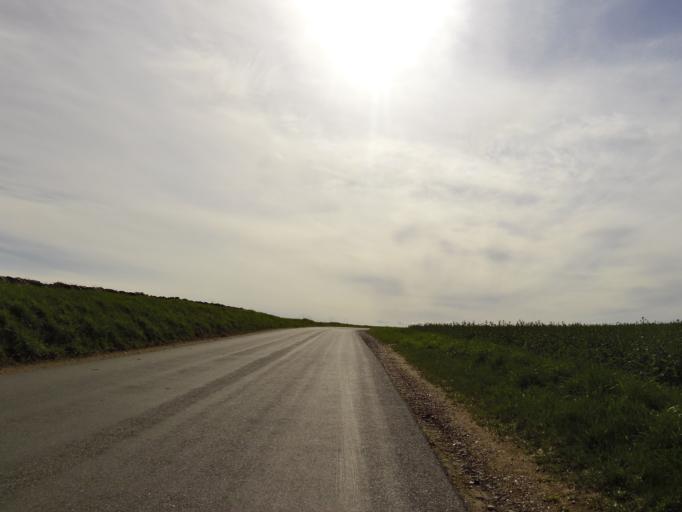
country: DK
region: Central Jutland
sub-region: Skive Kommune
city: Skive
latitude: 56.5452
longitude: 8.9625
